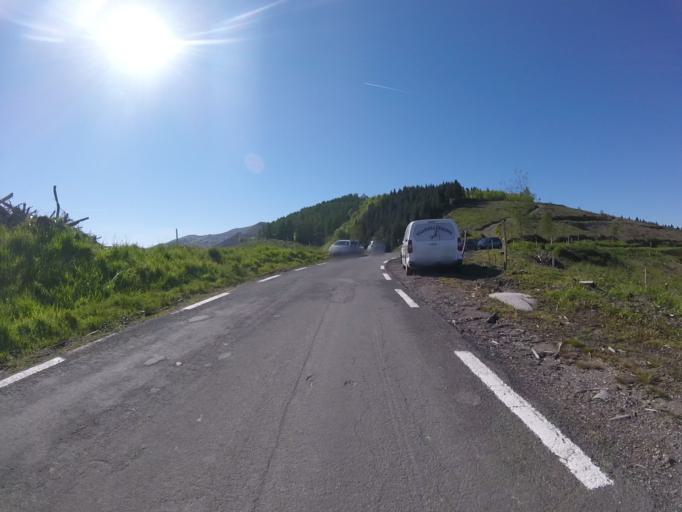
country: ES
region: Basque Country
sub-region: Provincia de Guipuzcoa
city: Errezil
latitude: 43.2030
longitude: -2.1977
